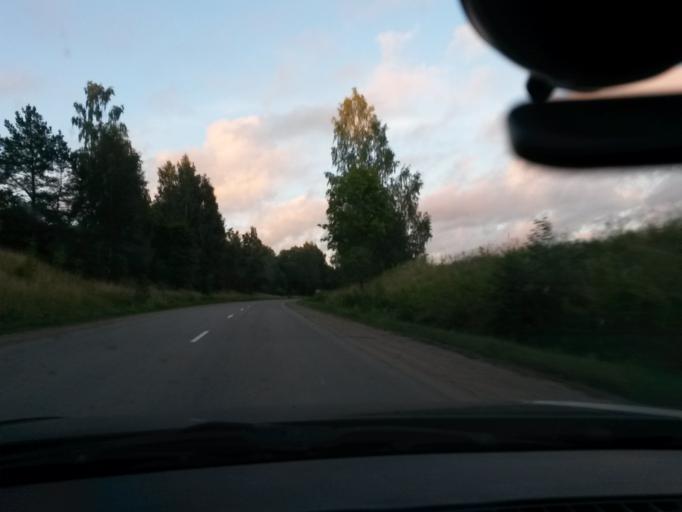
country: LV
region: Madonas Rajons
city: Madona
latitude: 56.8067
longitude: 26.0495
